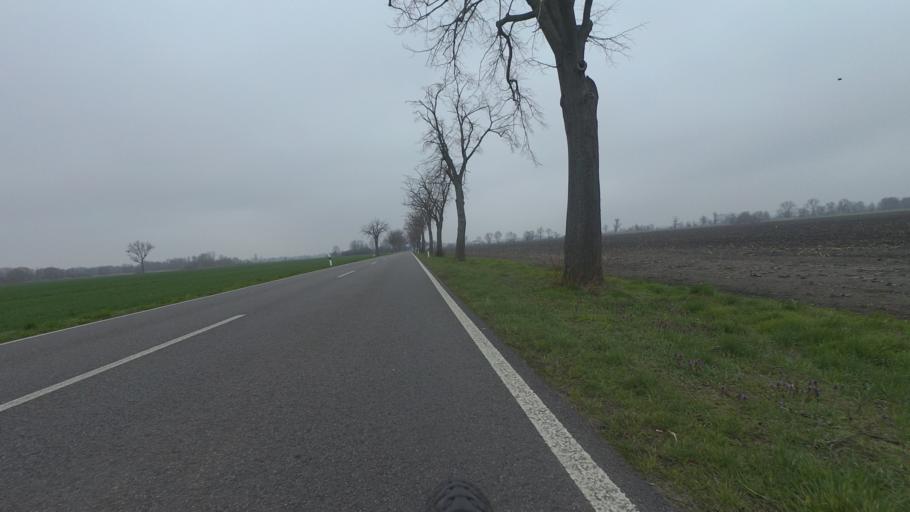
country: DE
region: Brandenburg
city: Nauen
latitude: 52.6186
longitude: 12.8734
